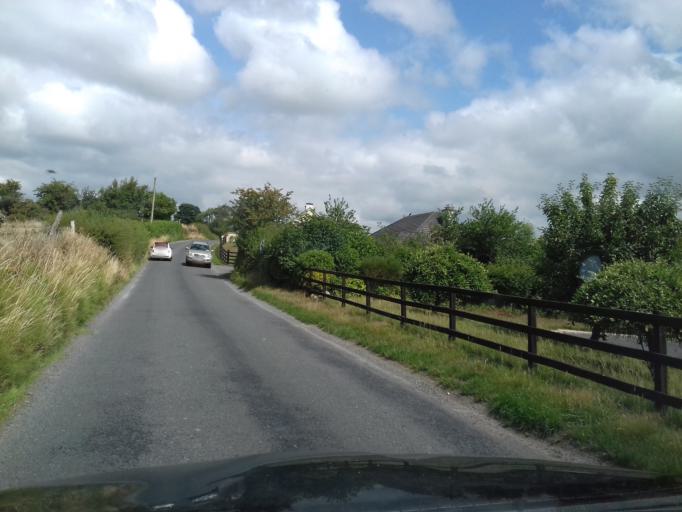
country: IE
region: Leinster
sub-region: Kilkenny
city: Graiguenamanagh
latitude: 52.6053
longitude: -6.9044
